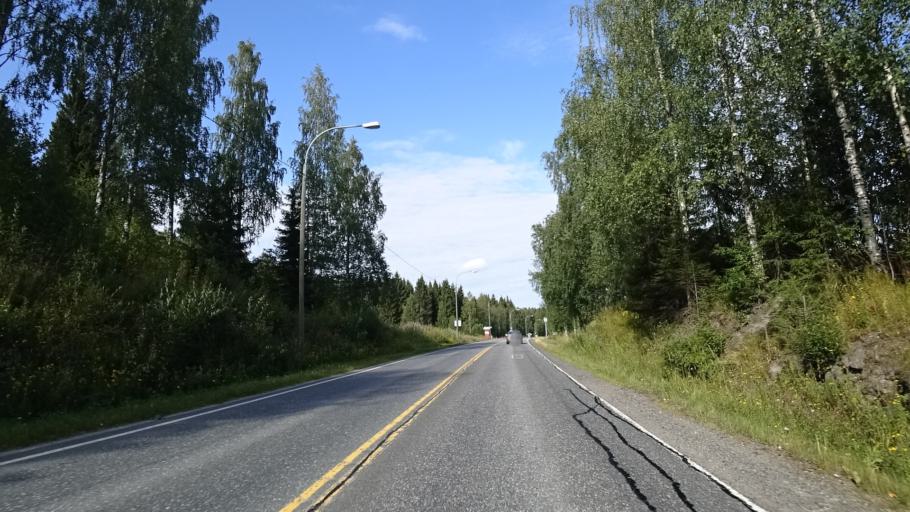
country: FI
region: North Karelia
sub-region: Joensuu
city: Eno
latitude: 62.7891
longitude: 30.0819
